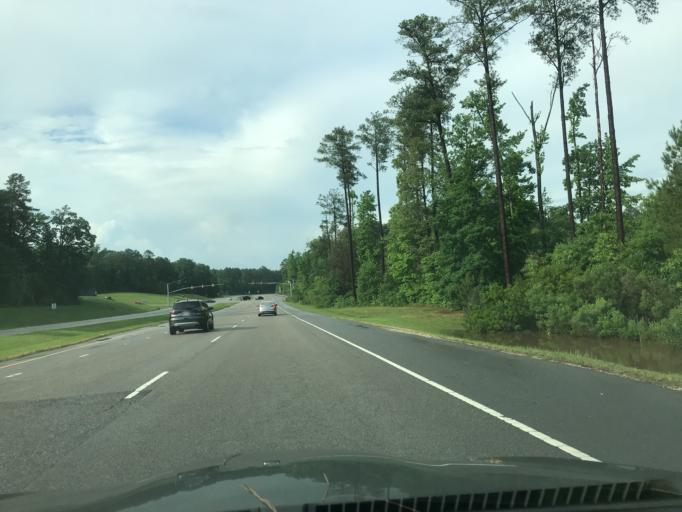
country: US
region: North Carolina
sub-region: Wake County
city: Morrisville
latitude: 35.8642
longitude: -78.8720
